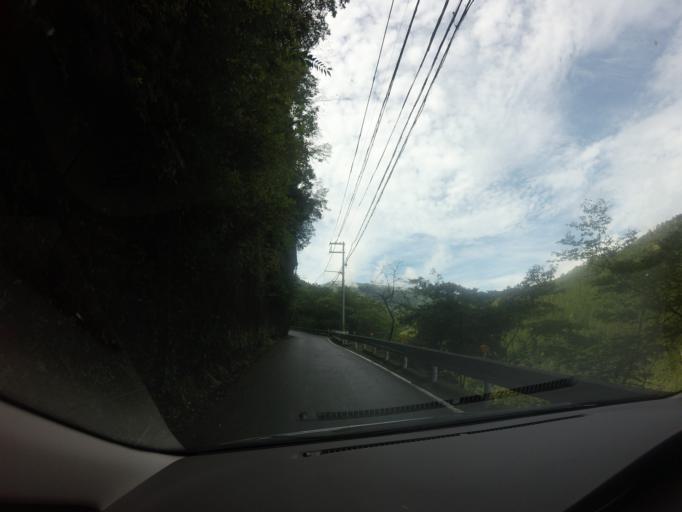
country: JP
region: Wakayama
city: Shingu
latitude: 33.9679
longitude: 135.8481
